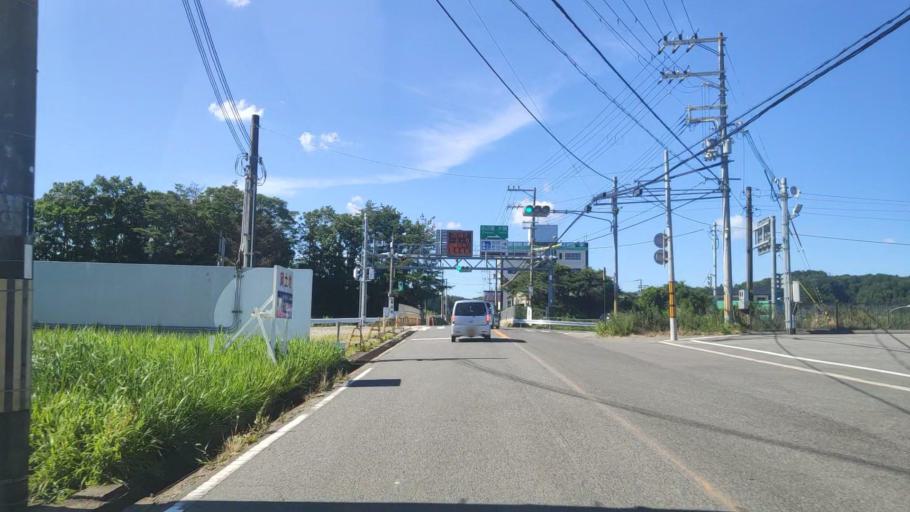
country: JP
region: Nara
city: Haibara-akanedai
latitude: 34.6094
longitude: 135.9588
